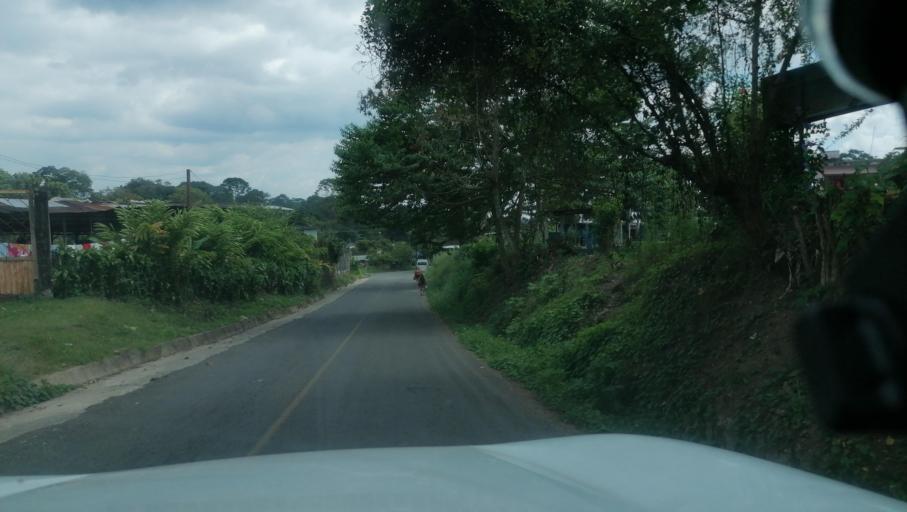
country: MX
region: Chiapas
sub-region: Cacahoatan
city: Benito Juarez
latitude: 15.0340
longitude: -92.1543
